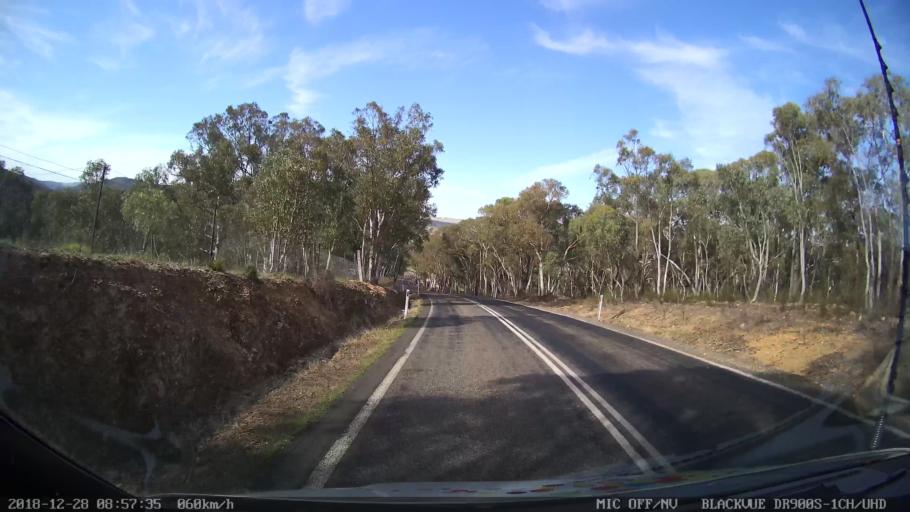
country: AU
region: New South Wales
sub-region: Upper Lachlan Shire
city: Crookwell
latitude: -34.1195
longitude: 149.3341
